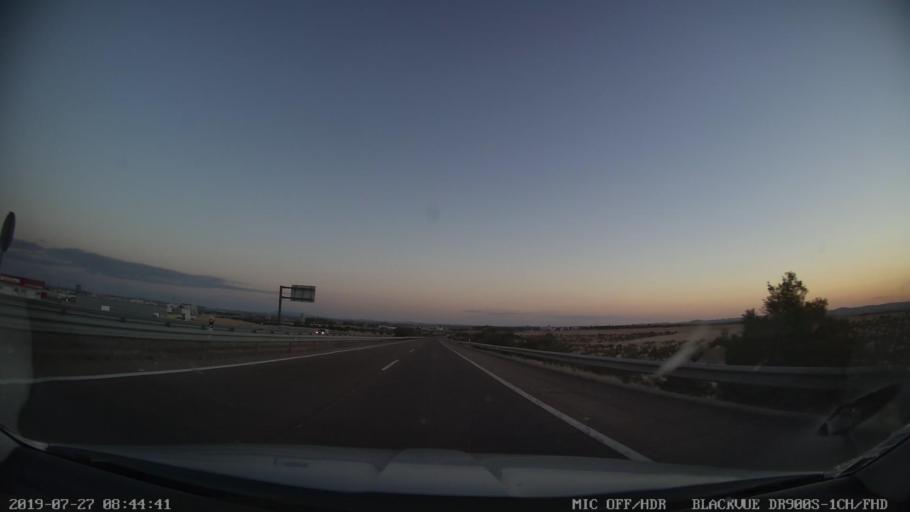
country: ES
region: Extremadura
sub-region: Provincia de Badajoz
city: Badajoz
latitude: 38.8998
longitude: -7.0024
